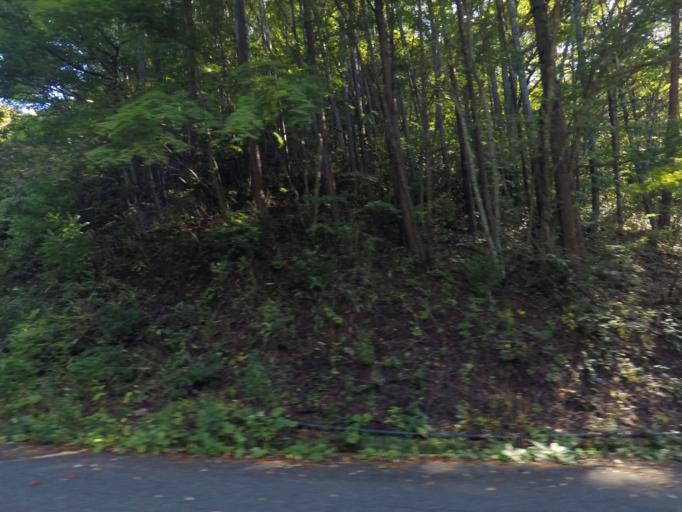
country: JP
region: Nagano
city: Tatsuno
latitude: 35.9655
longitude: 137.7743
